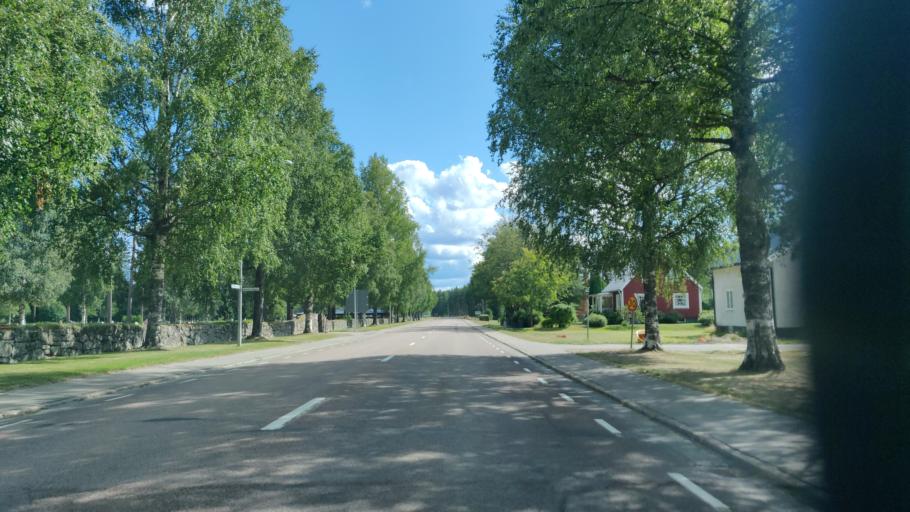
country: SE
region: Vaermland
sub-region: Hagfors Kommun
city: Ekshaerad
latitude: 60.1713
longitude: 13.4969
